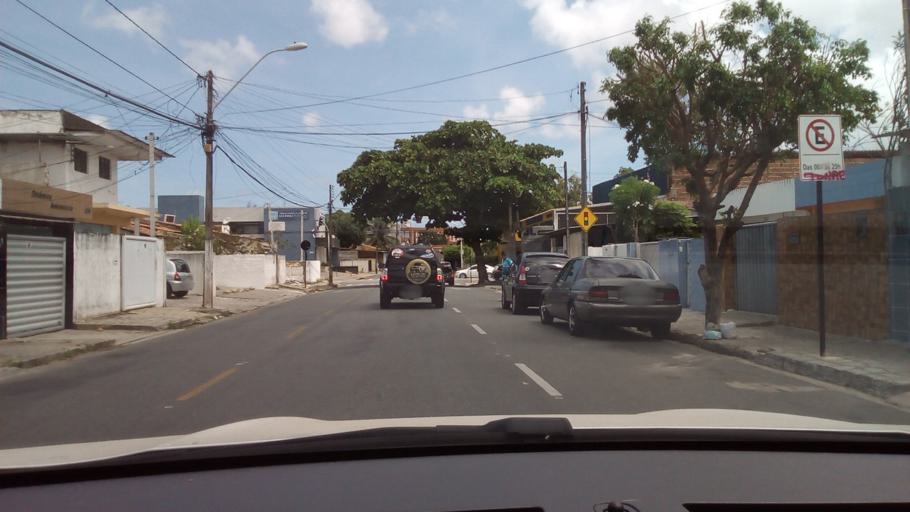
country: BR
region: Paraiba
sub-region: Joao Pessoa
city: Joao Pessoa
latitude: -7.1253
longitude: -34.8607
